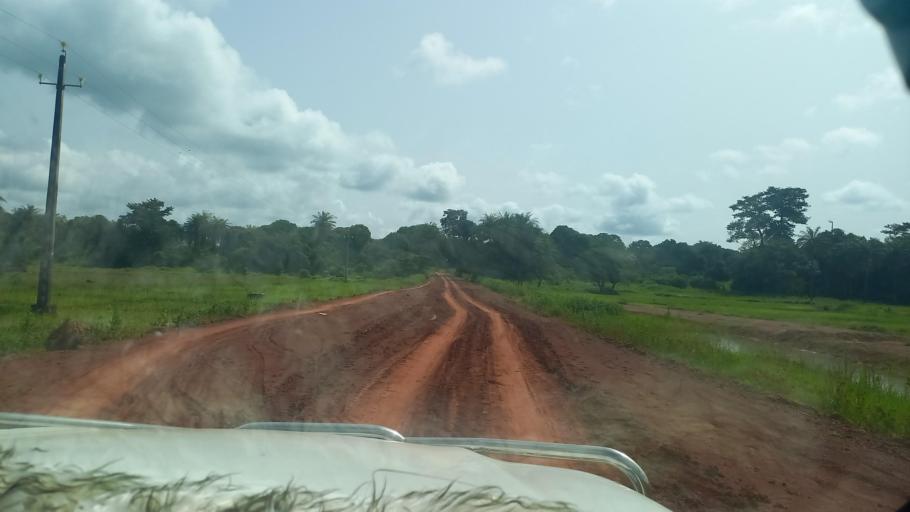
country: SN
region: Ziguinchor
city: Bignona
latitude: 12.7548
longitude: -16.2728
